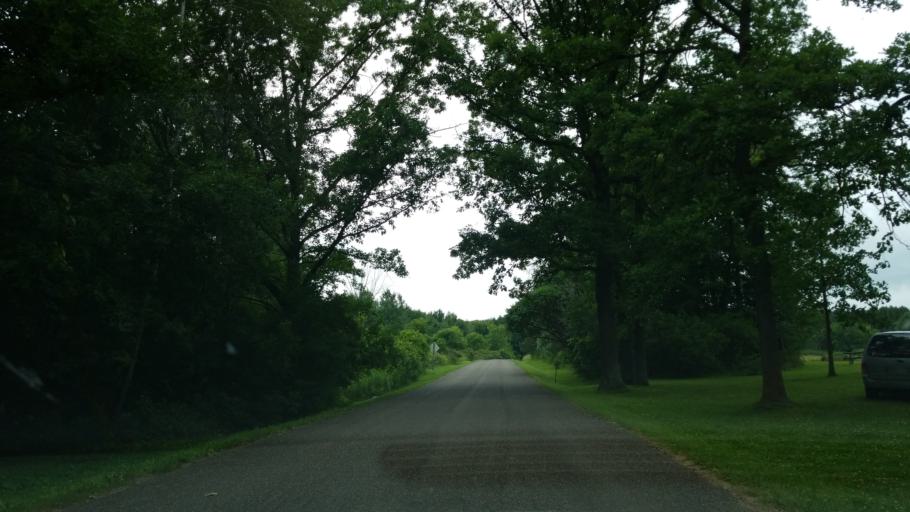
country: US
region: Wisconsin
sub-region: Saint Croix County
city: Glenwood City
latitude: 45.0056
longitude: -92.1716
